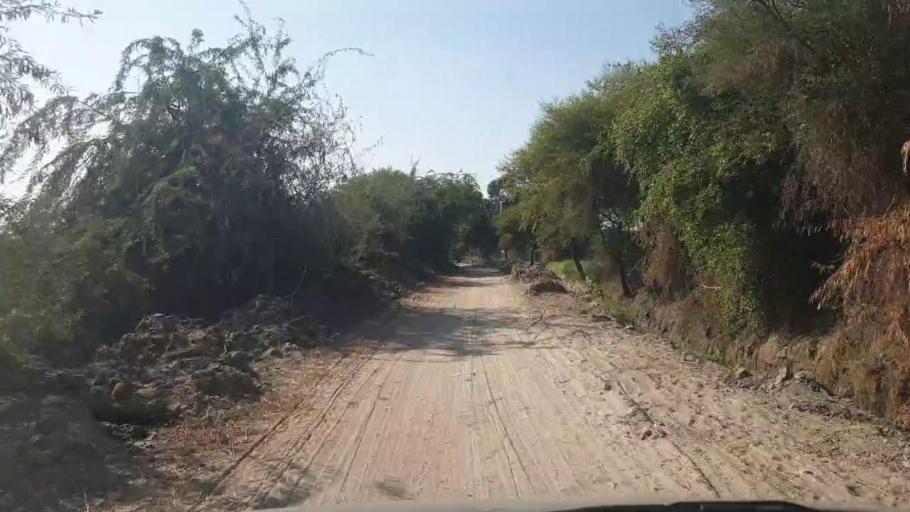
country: PK
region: Sindh
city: Badin
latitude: 24.5802
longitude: 68.7946
